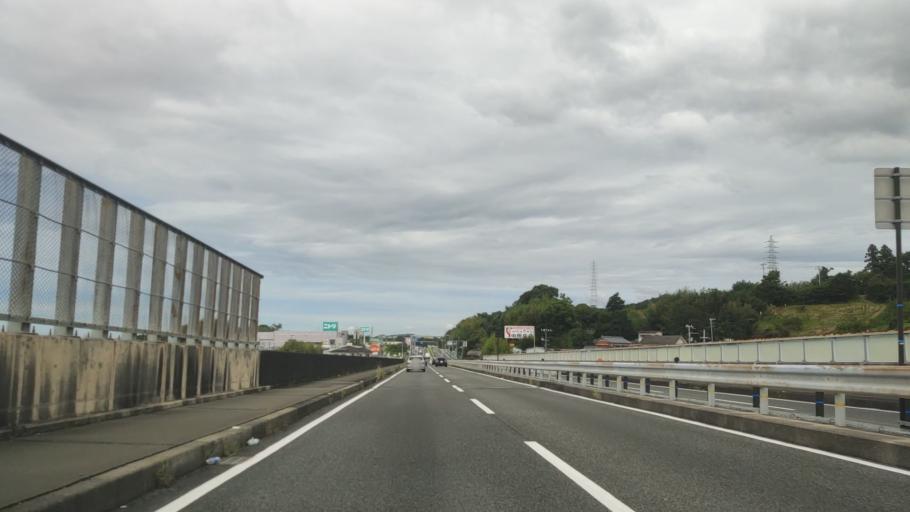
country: JP
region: Wakayama
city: Tanabe
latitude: 33.7186
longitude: 135.4070
